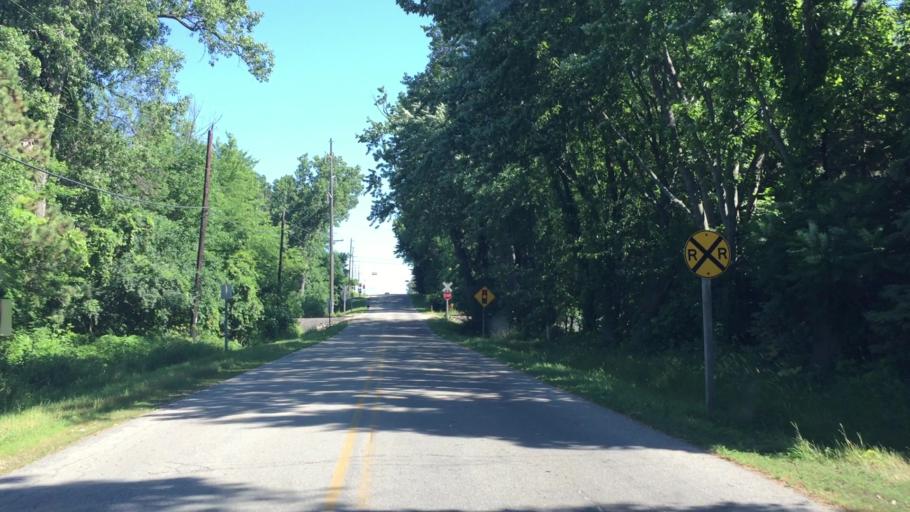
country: US
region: Wisconsin
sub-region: Outagamie County
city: Kimberly
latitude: 44.2052
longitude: -88.3636
